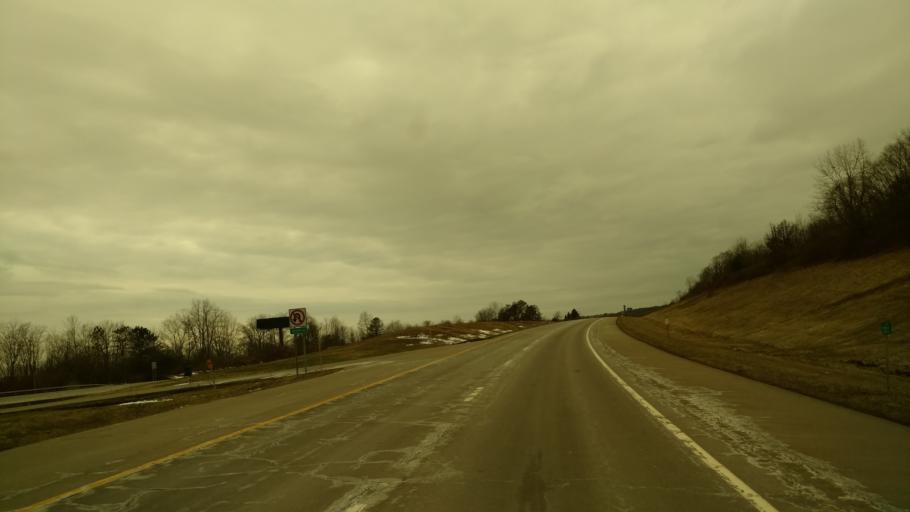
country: US
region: New York
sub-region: Chautauqua County
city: Celoron
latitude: 42.1211
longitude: -79.2589
